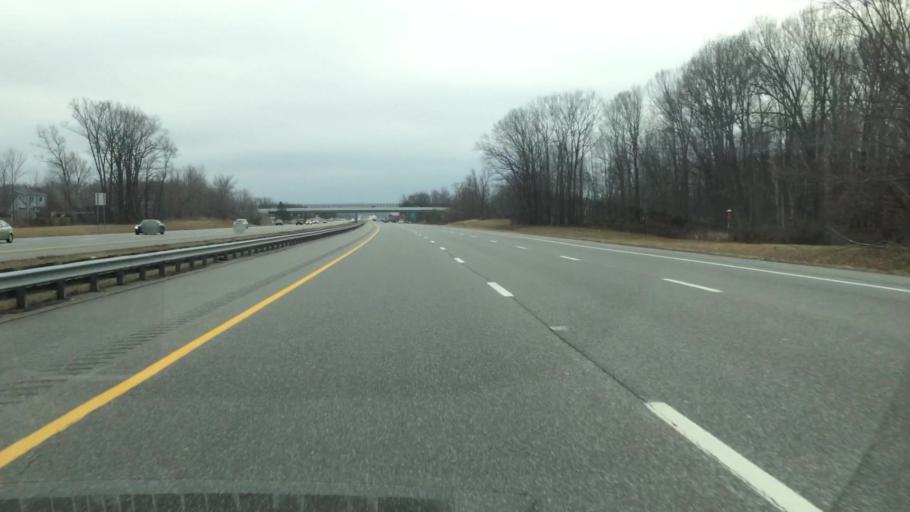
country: US
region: Ohio
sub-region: Cuyahoga County
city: Strongsville
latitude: 41.2798
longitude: -81.8073
